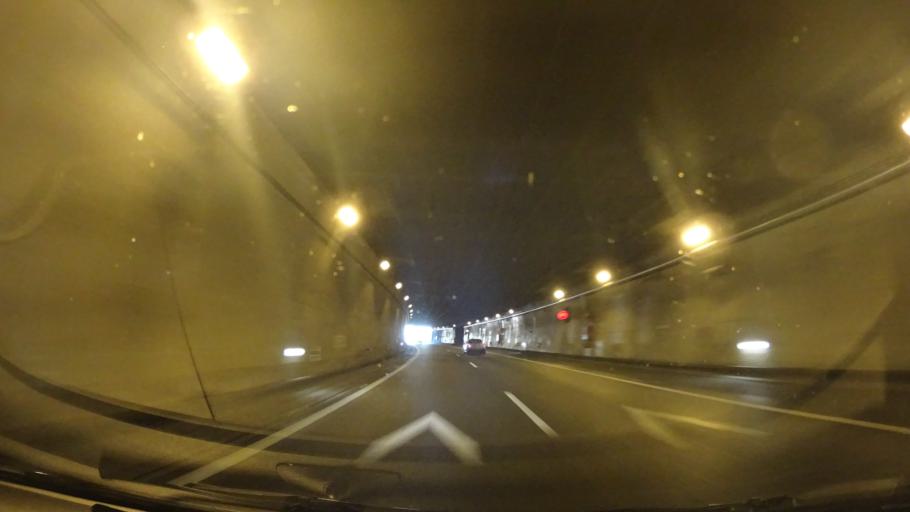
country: ES
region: Madrid
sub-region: Provincia de Madrid
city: Guadarrama
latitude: 40.7168
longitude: -4.1593
